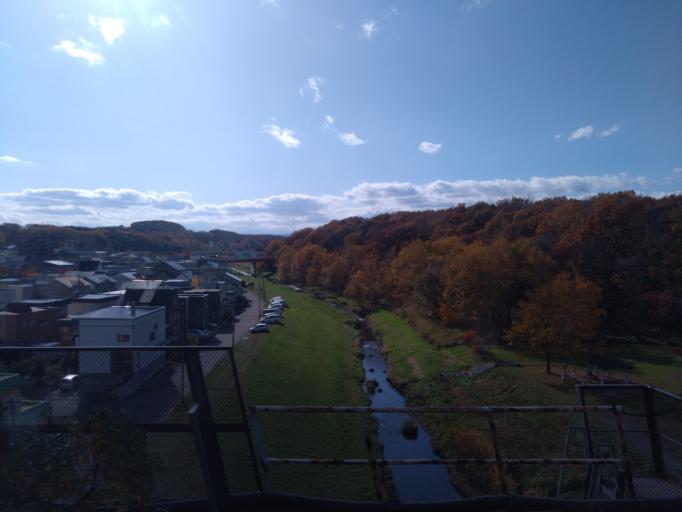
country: JP
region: Hokkaido
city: Kitahiroshima
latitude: 42.9878
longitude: 141.5600
